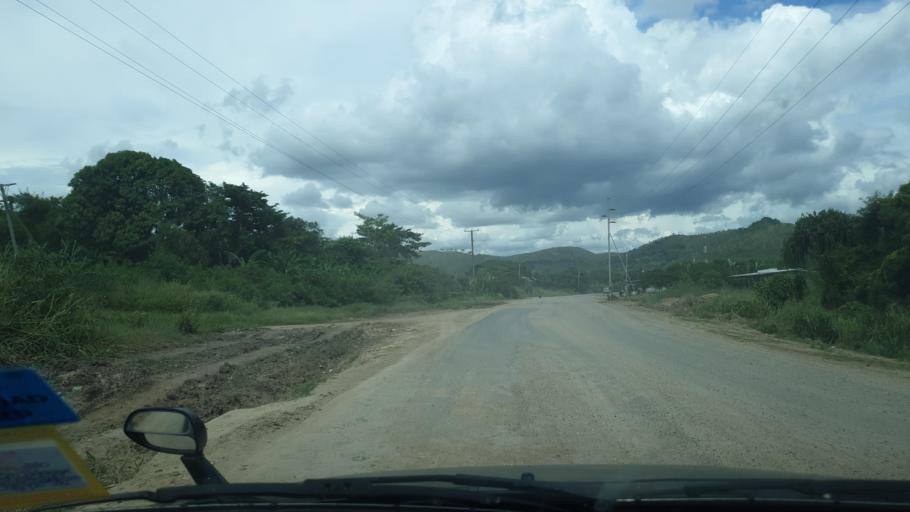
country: PG
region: National Capital
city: Port Moresby
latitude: -9.4173
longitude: 147.1244
